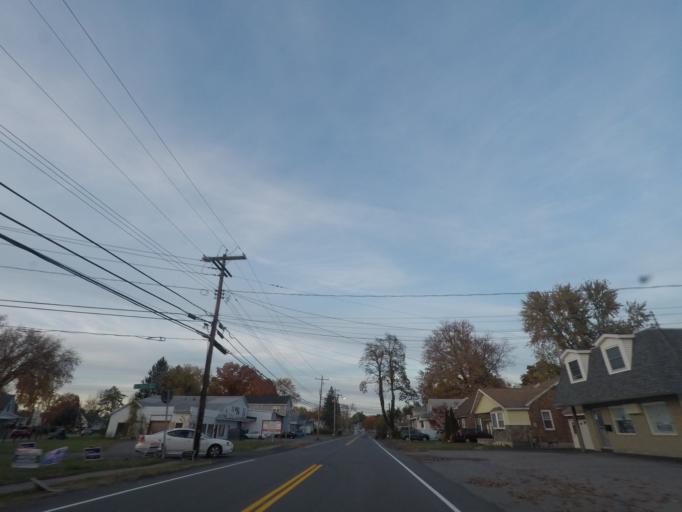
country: US
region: New York
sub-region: Schenectady County
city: Rotterdam
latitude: 42.7794
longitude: -73.9719
